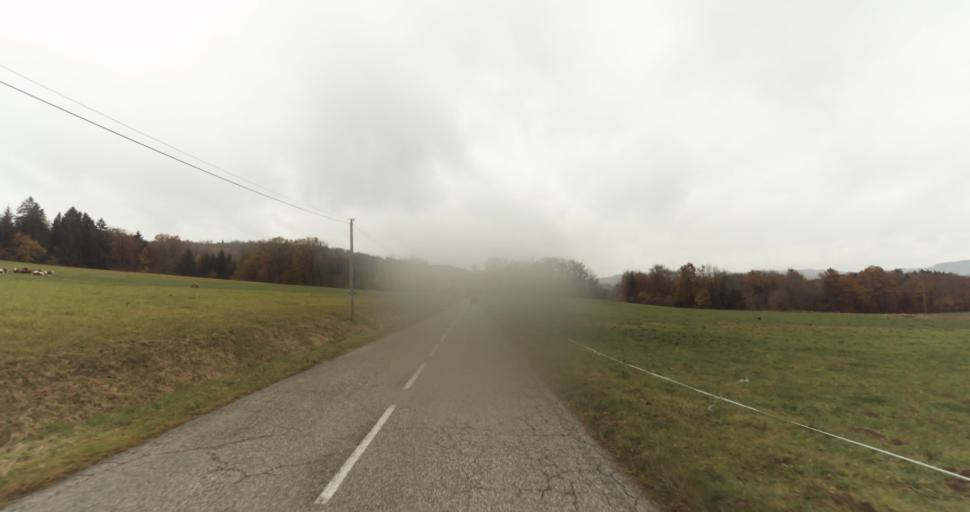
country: FR
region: Rhone-Alpes
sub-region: Departement de la Haute-Savoie
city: Saint-Martin-Bellevue
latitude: 45.9844
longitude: 6.1552
